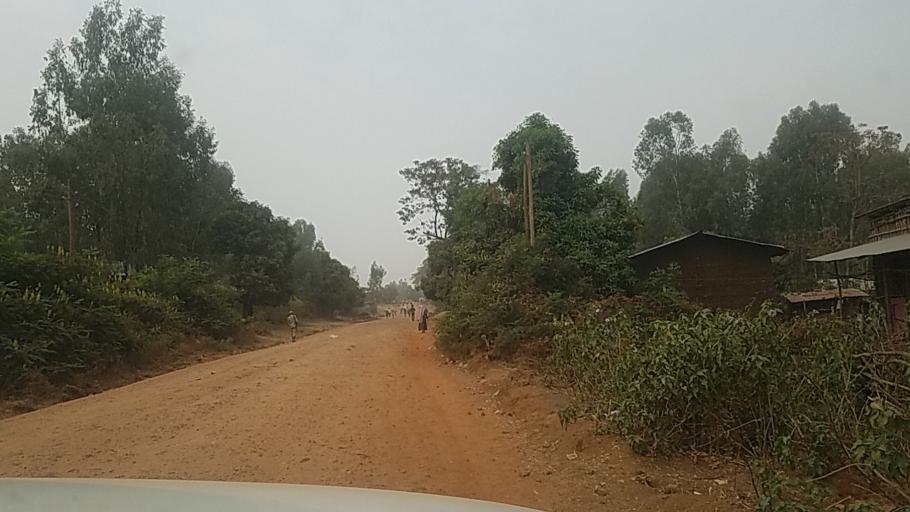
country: ET
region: Amhara
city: Bure
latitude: 10.8541
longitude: 36.3535
